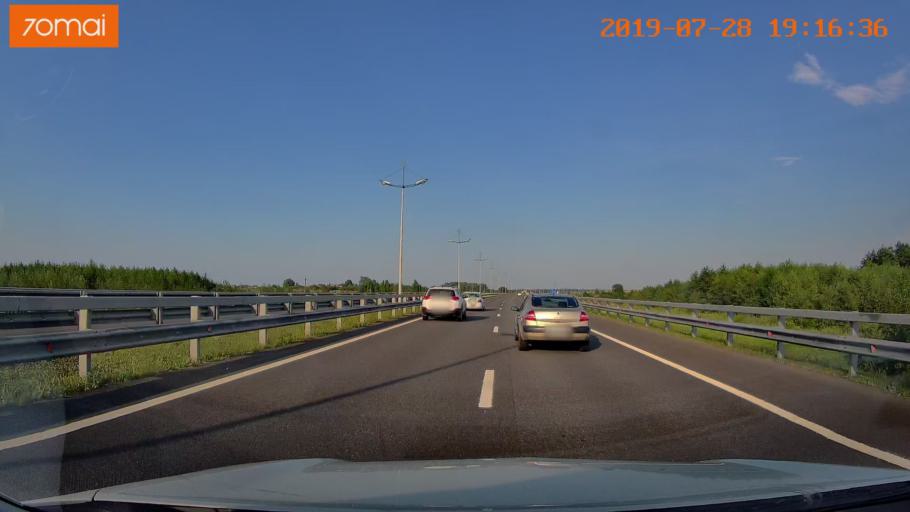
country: RU
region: Kaliningrad
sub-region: Zelenogradskiy Rayon
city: Zelenogradsk
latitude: 54.9228
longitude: 20.3791
